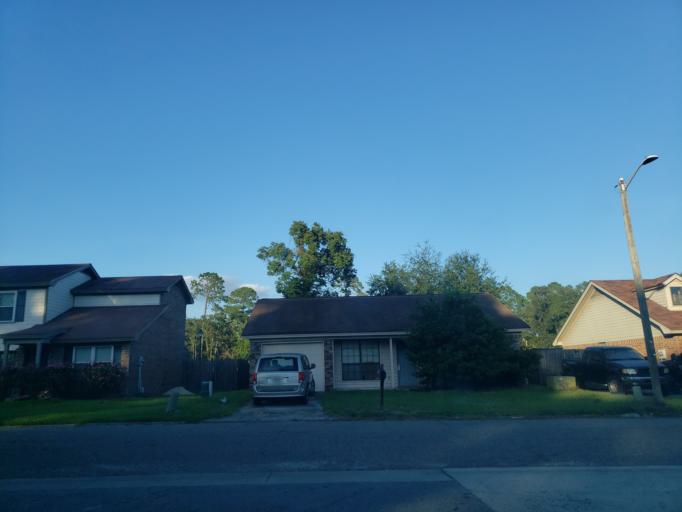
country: US
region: Georgia
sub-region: Chatham County
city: Isle of Hope
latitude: 31.9916
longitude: -81.0717
